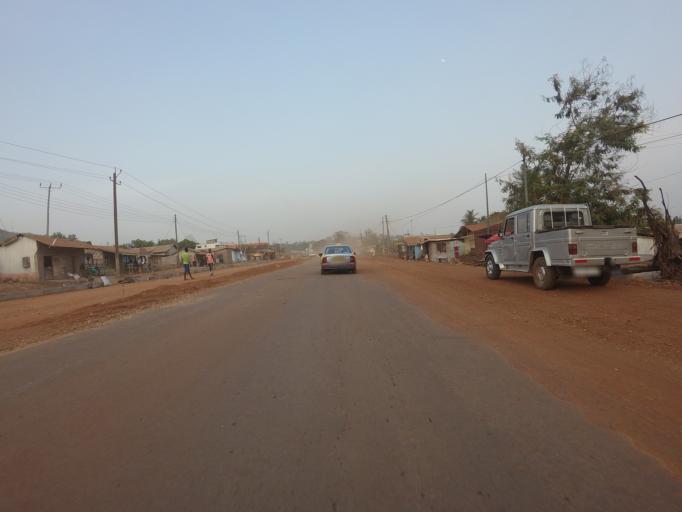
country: GH
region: Volta
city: Ho
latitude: 6.5969
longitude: 0.4448
